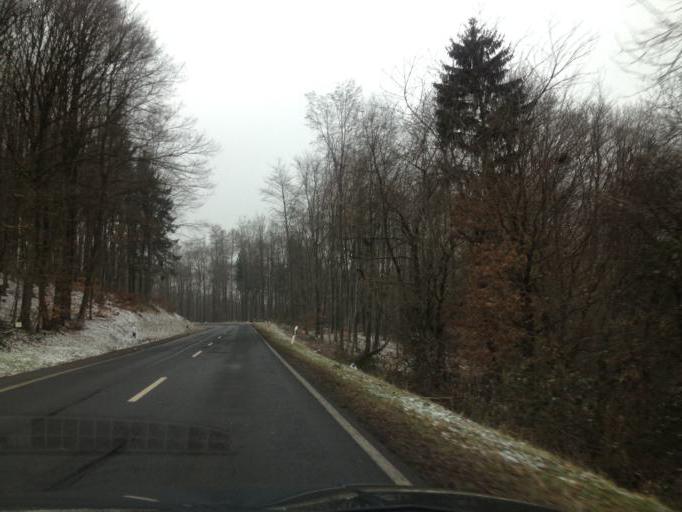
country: DE
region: Saarland
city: Bexbach
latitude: 49.3884
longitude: 7.2551
